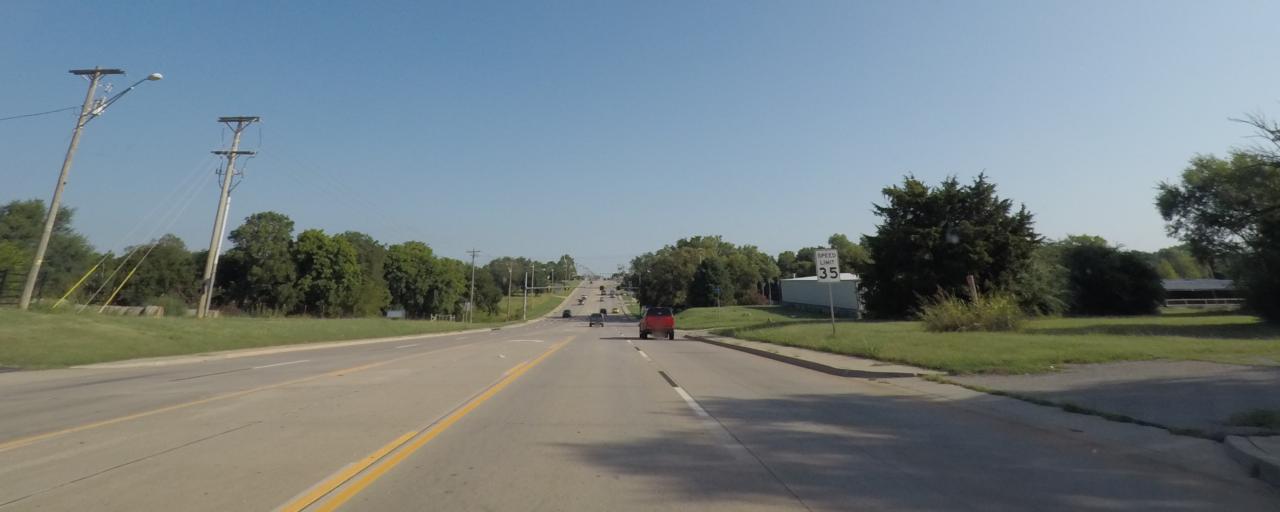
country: US
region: Oklahoma
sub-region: McClain County
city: Newcastle
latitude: 35.2500
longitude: -97.6002
